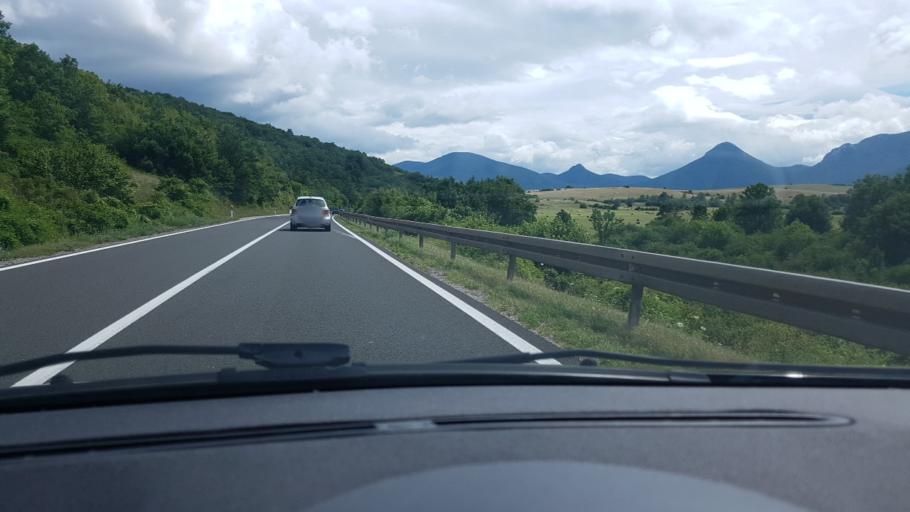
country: HR
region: Zadarska
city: Gracac
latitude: 44.4985
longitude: 15.7637
